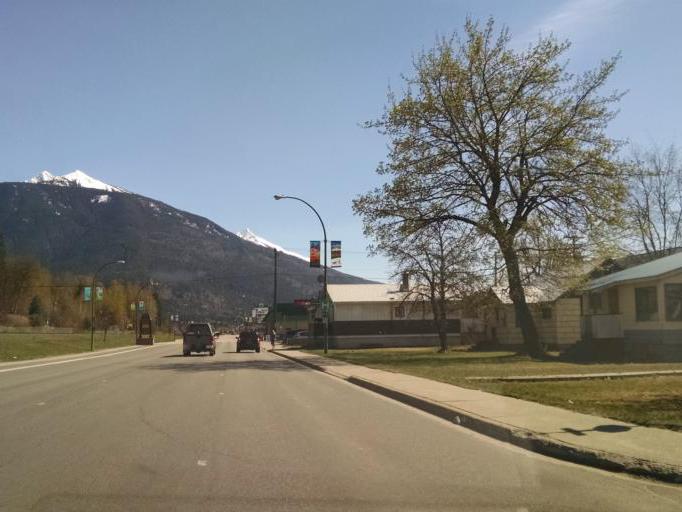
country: CA
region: British Columbia
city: Revelstoke
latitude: 51.0031
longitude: -118.2005
